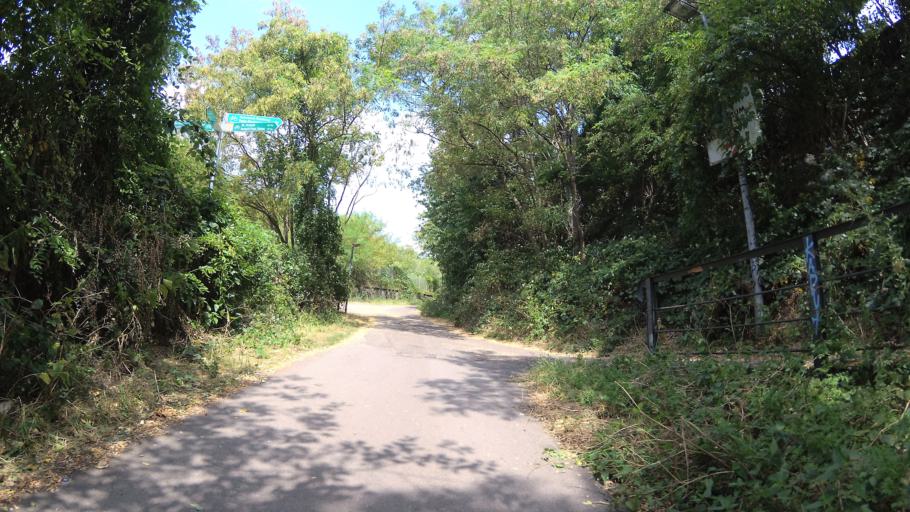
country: DE
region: Saarland
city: Saarbrucken
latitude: 49.2354
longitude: 6.9613
